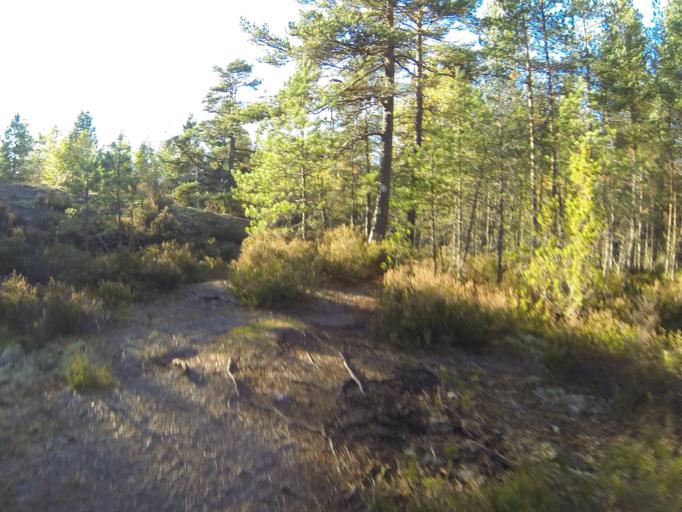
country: FI
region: Varsinais-Suomi
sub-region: Salo
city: Saerkisalo
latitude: 60.2185
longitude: 22.9312
